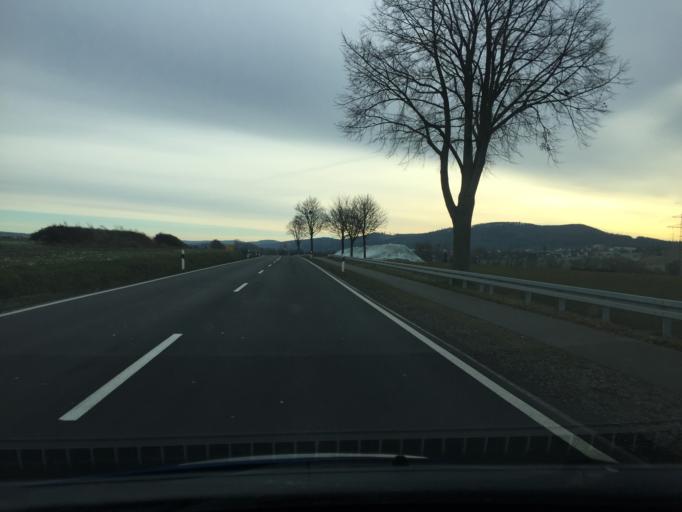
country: DE
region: Lower Saxony
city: Luerdissen
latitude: 51.9463
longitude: 9.6251
